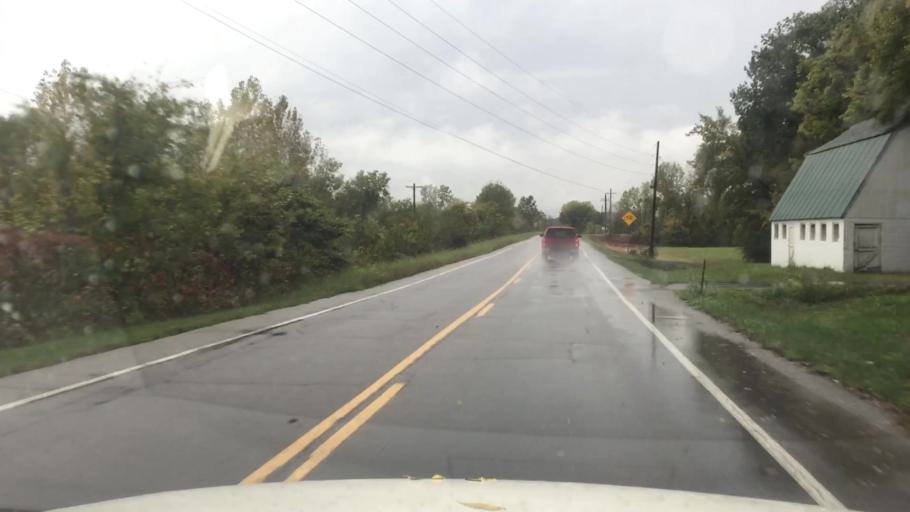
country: US
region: Missouri
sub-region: Boone County
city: Columbia
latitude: 38.8858
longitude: -92.4393
